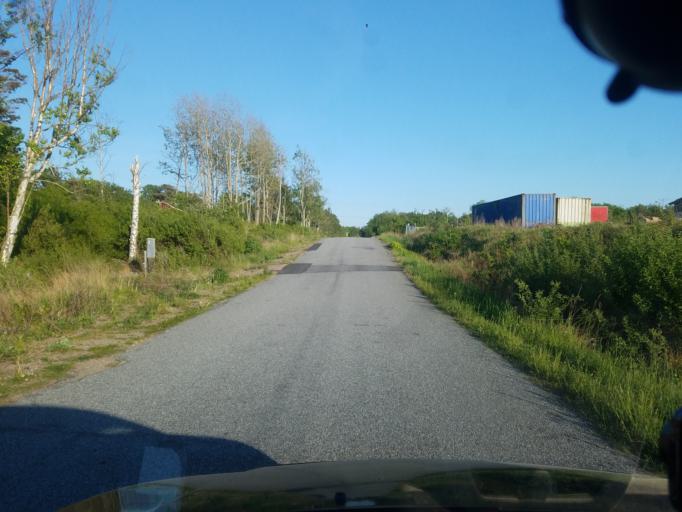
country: SE
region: Vaestra Goetaland
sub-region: Lysekils Kommun
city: Lysekil
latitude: 58.2950
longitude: 11.4503
